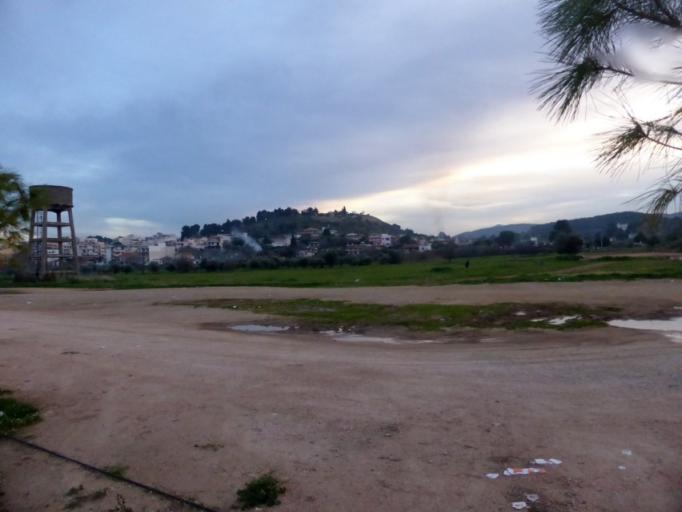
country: GR
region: Attica
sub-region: Nomarchia Anatolikis Attikis
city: Skala Oropou
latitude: 38.3211
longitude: 23.7843
